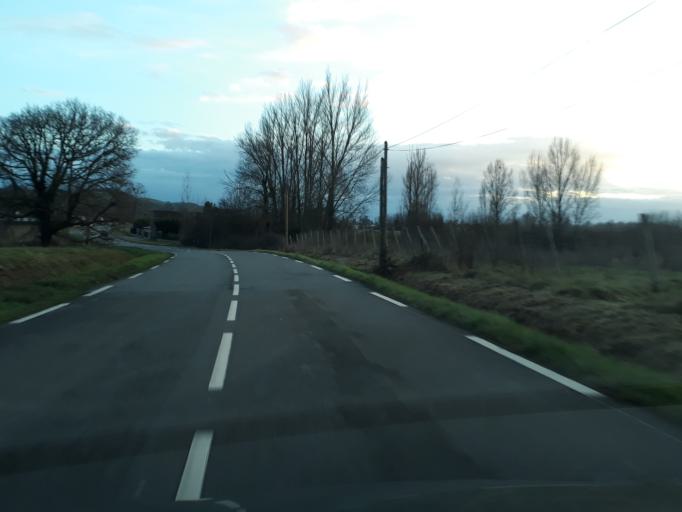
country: FR
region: Midi-Pyrenees
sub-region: Departement de la Haute-Garonne
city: Marquefave
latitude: 43.3265
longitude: 1.2461
